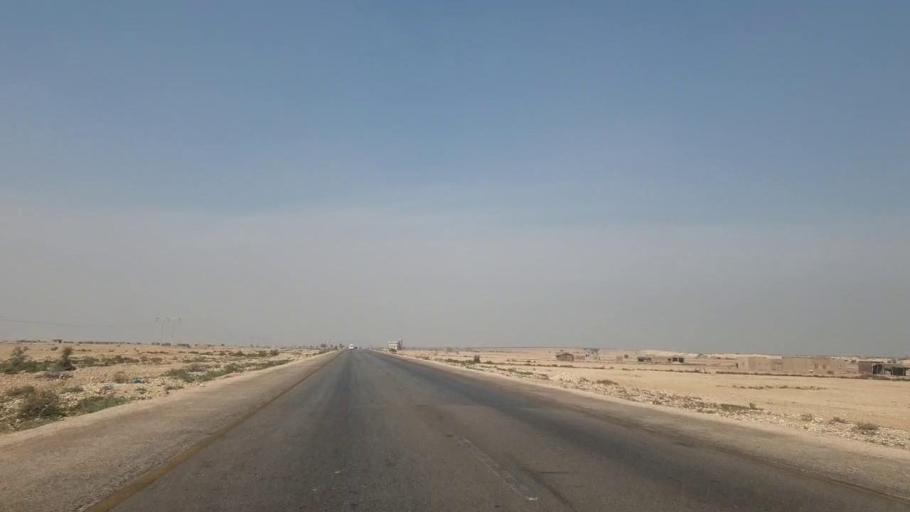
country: PK
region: Sindh
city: Hala
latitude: 25.8483
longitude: 68.2608
